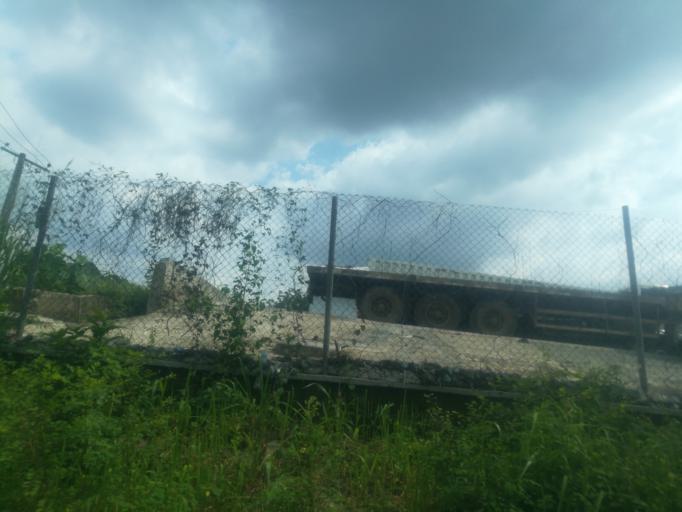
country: NG
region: Oyo
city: Ibadan
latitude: 7.4079
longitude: 3.8697
